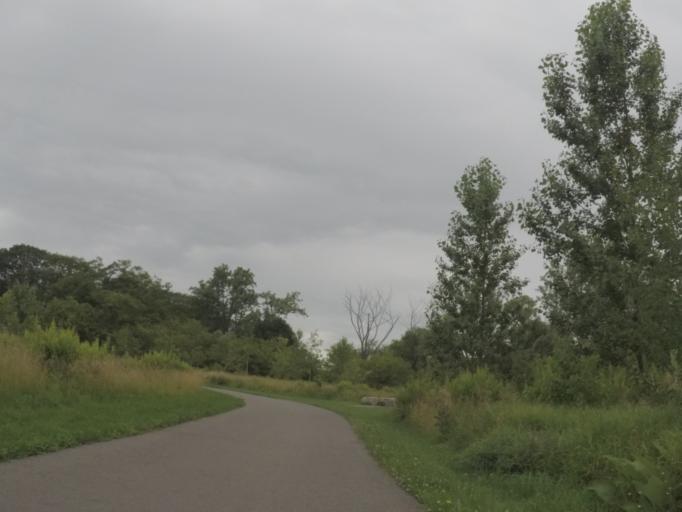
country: CA
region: Ontario
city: Toronto
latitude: 43.6362
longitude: -79.4786
